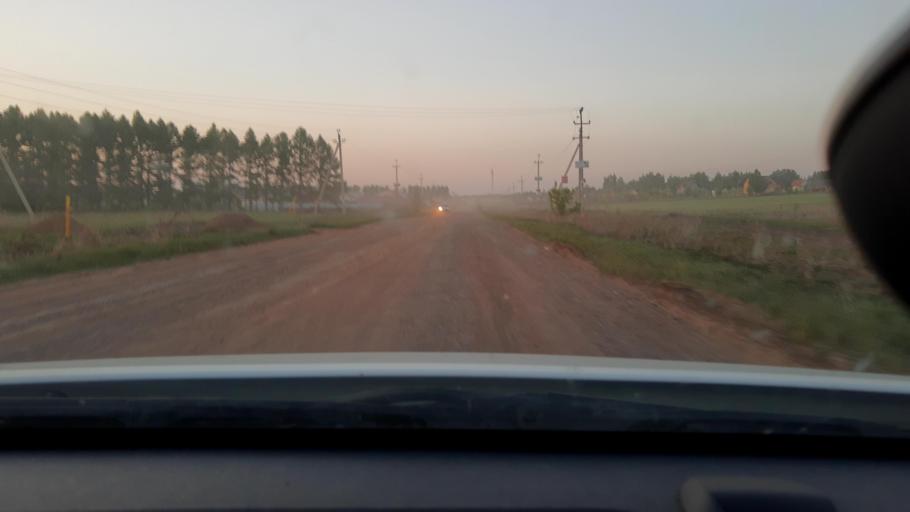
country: RU
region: Bashkortostan
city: Avdon
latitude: 54.5123
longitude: 55.8207
